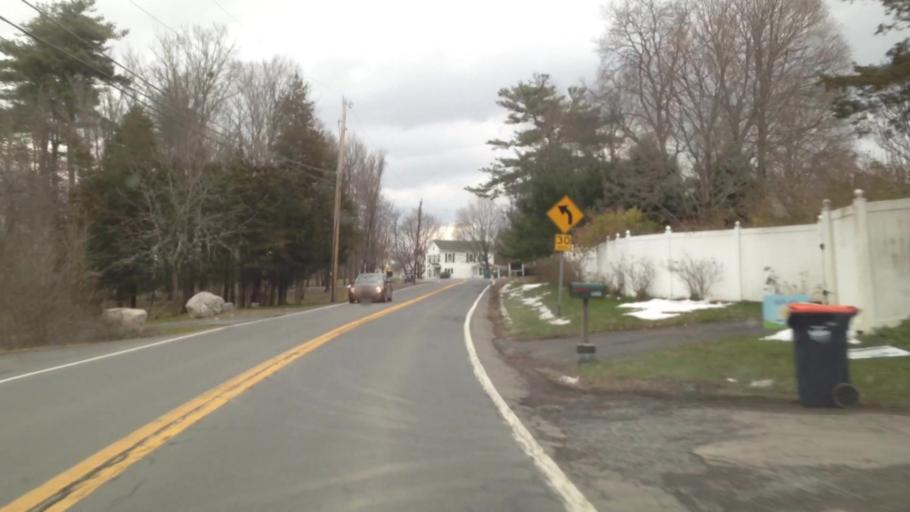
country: US
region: New York
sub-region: Ulster County
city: Glasco
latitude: 42.0218
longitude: -73.9562
